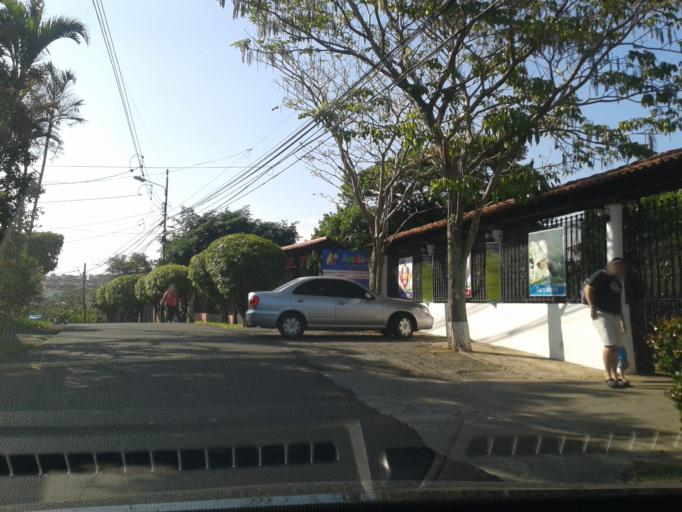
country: CR
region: Heredia
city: Llorente
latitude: 10.0054
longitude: -84.1474
